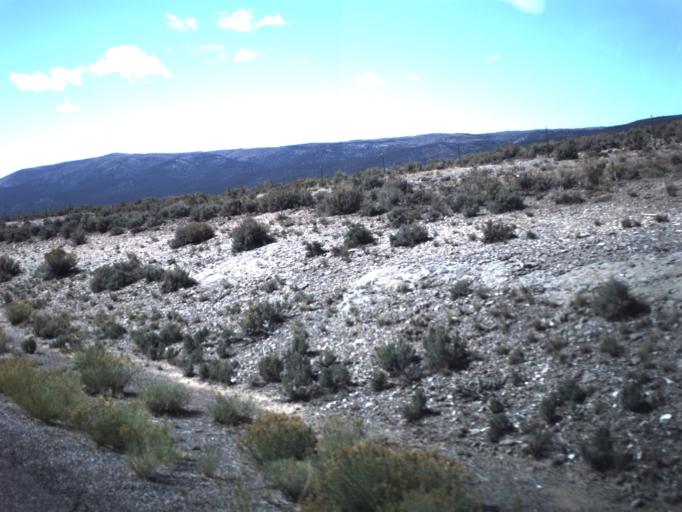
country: US
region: Utah
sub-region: Piute County
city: Junction
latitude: 38.3011
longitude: -111.9711
